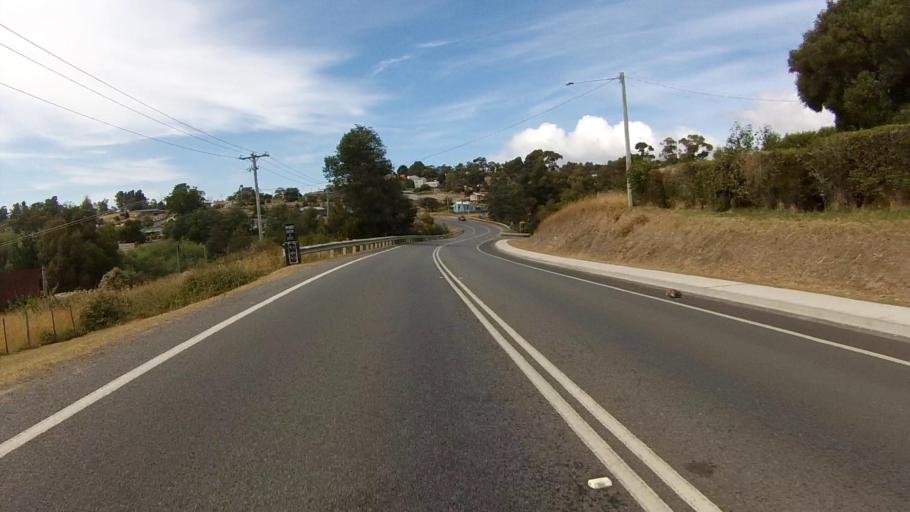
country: AU
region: Tasmania
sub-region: Kingborough
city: Kettering
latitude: -43.1263
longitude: 147.2463
